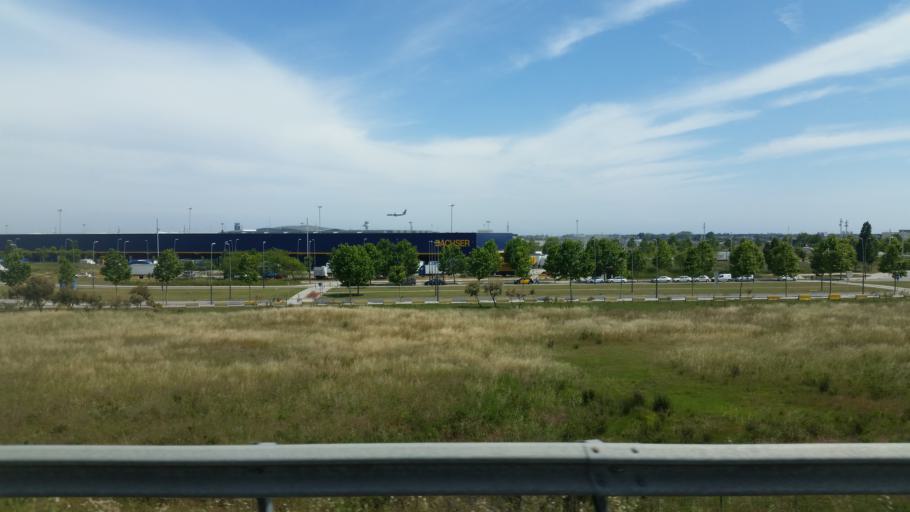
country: ES
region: Catalonia
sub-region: Provincia de Barcelona
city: Viladecans
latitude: 41.3011
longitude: 2.0543
